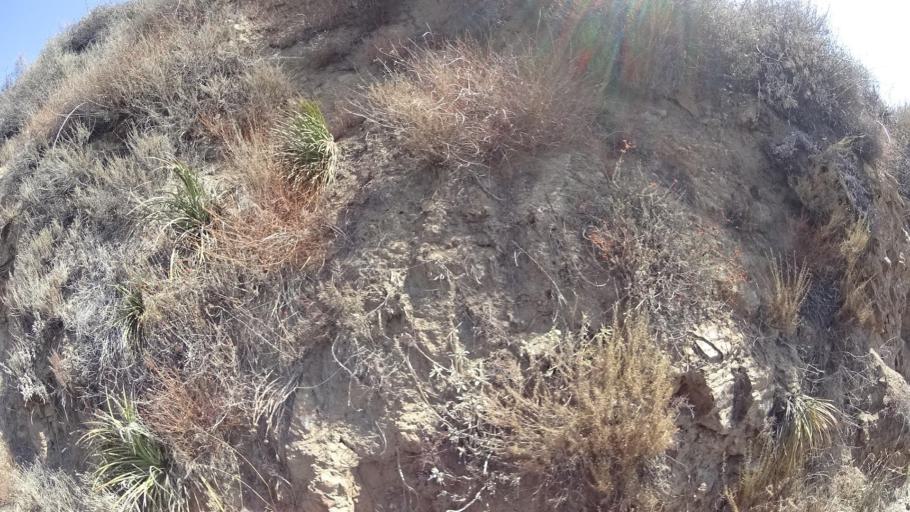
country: US
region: California
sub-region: Riverside County
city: Aguanga
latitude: 33.3345
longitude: -116.9418
